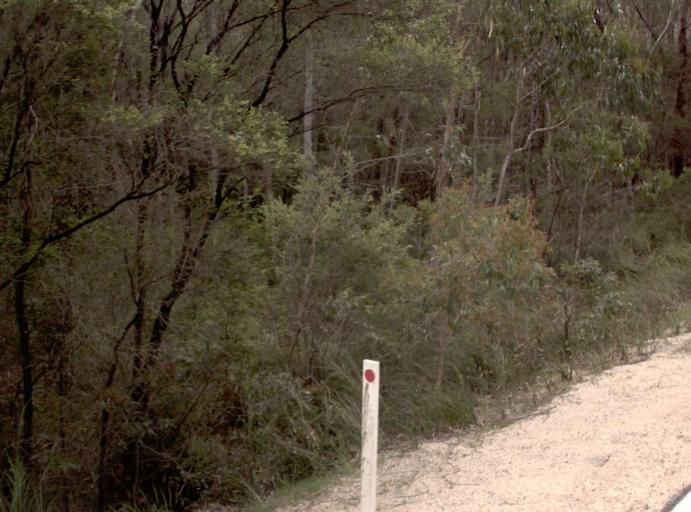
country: AU
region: New South Wales
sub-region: Bega Valley
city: Eden
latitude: -37.4408
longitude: 149.6438
